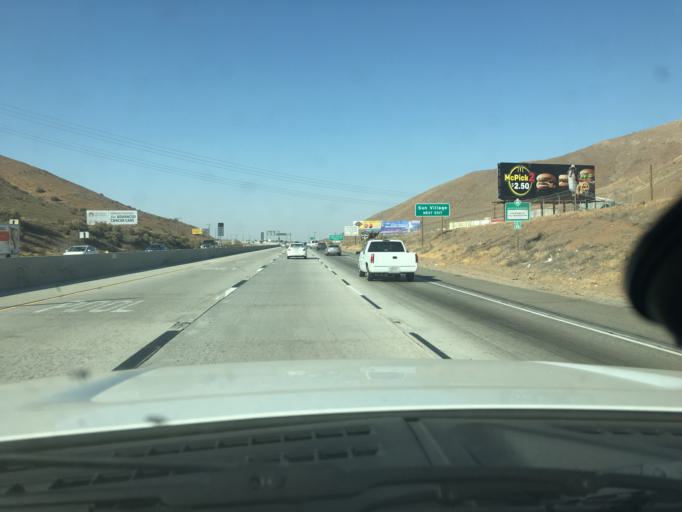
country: US
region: California
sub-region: Los Angeles County
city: Vincent
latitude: 34.5022
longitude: -118.1186
